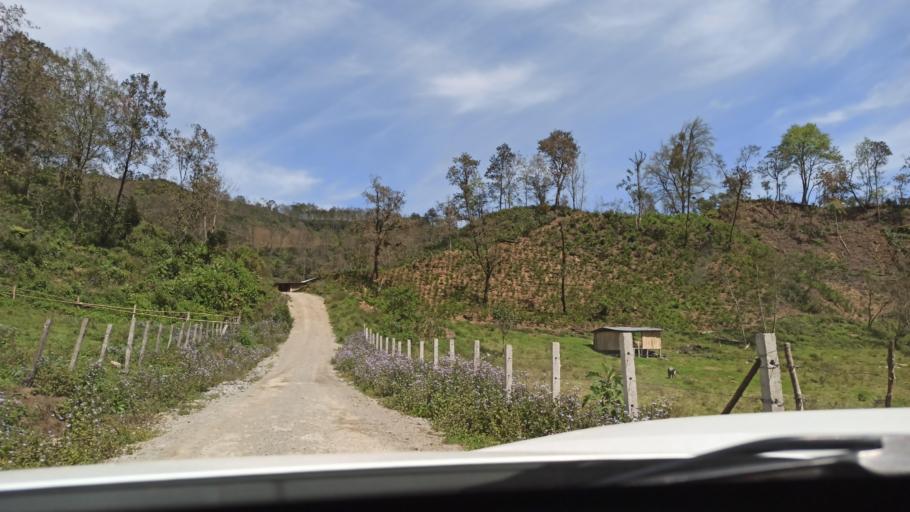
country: MX
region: Veracruz
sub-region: La Perla
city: Metlac Hernandez (Metlac Primero)
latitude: 18.9758
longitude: -97.1070
